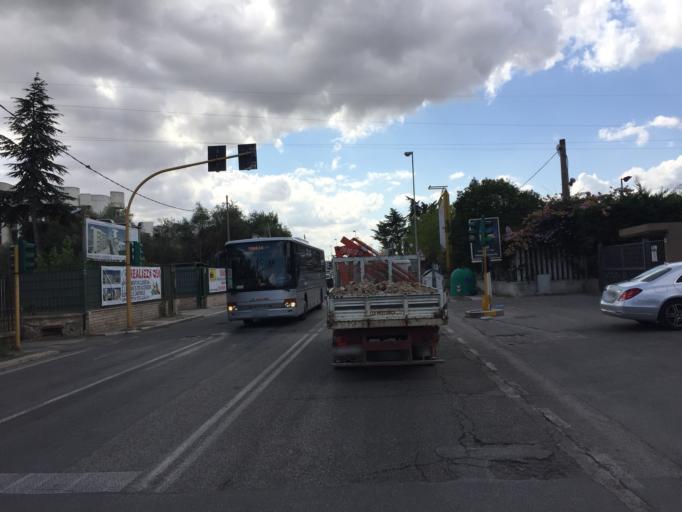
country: IT
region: Apulia
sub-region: Provincia di Bari
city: Bari
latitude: 41.0937
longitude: 16.8833
